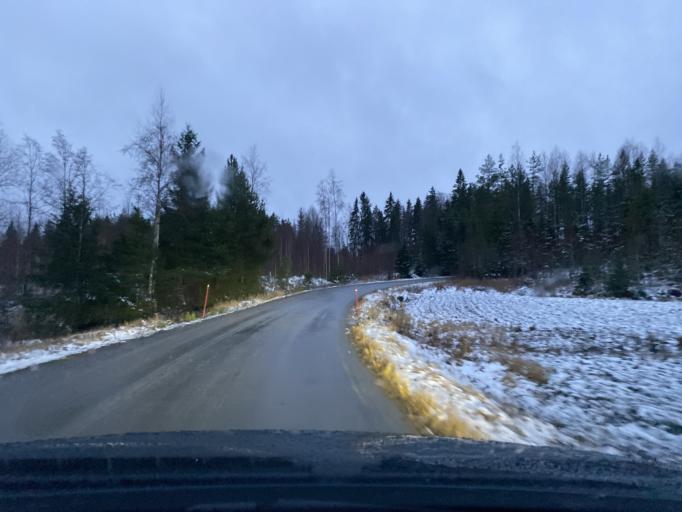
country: FI
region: Pirkanmaa
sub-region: Lounais-Pirkanmaa
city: Punkalaidun
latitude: 61.1553
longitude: 22.9658
